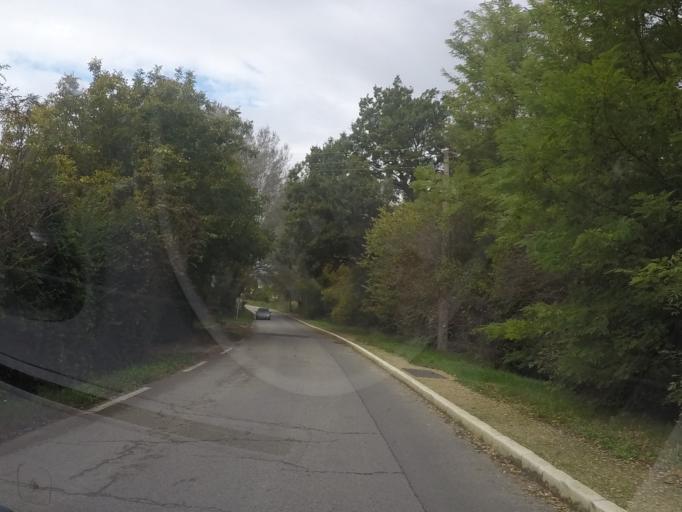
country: FR
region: Provence-Alpes-Cote d'Azur
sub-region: Departement du Vaucluse
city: Ansouis
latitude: 43.7394
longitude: 5.4612
